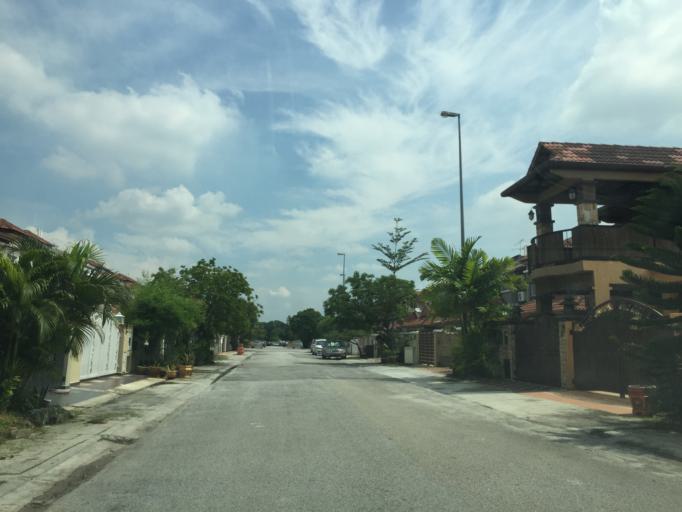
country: MY
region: Selangor
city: Klang
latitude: 2.9886
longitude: 101.4388
